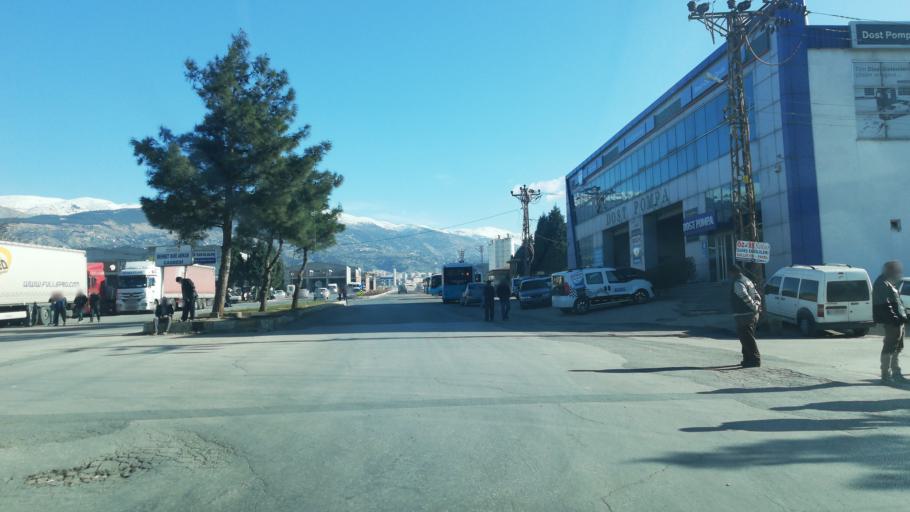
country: TR
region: Kahramanmaras
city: Kahramanmaras
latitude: 37.5659
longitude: 36.9629
